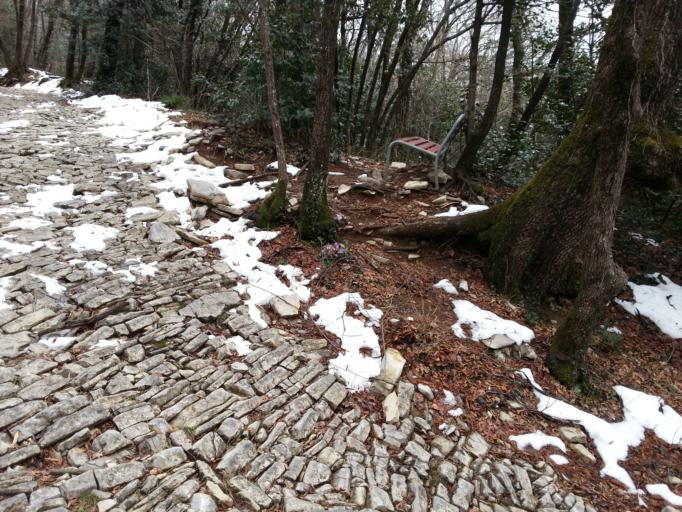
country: CH
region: Ticino
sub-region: Mendrisio District
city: Riva San Vitale
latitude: 45.8991
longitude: 8.9501
